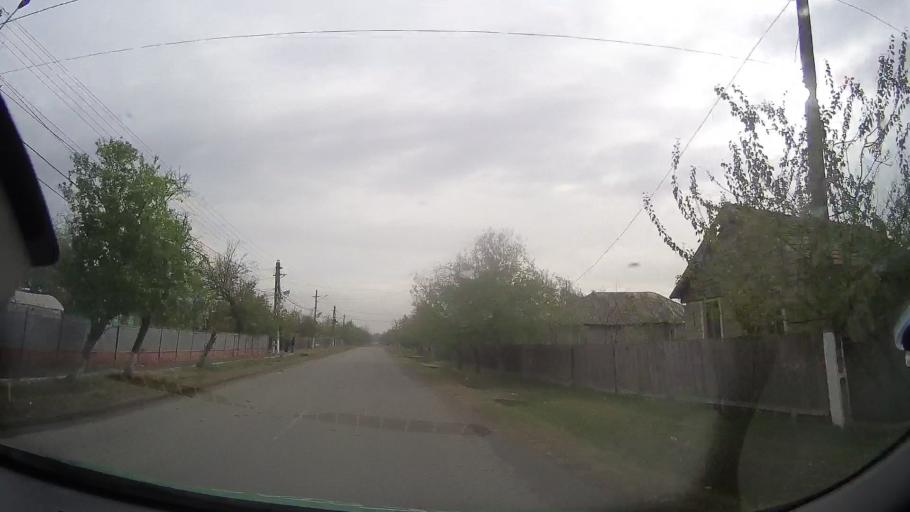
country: RO
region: Prahova
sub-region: Comuna Dumbrava
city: Dumbrava
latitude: 44.8686
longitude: 26.1968
